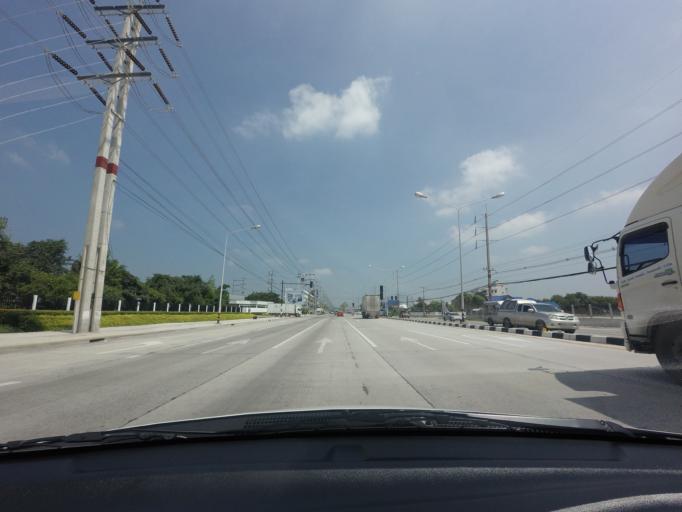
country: TH
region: Chachoengsao
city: Ban Pho
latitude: 13.6154
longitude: 101.0278
